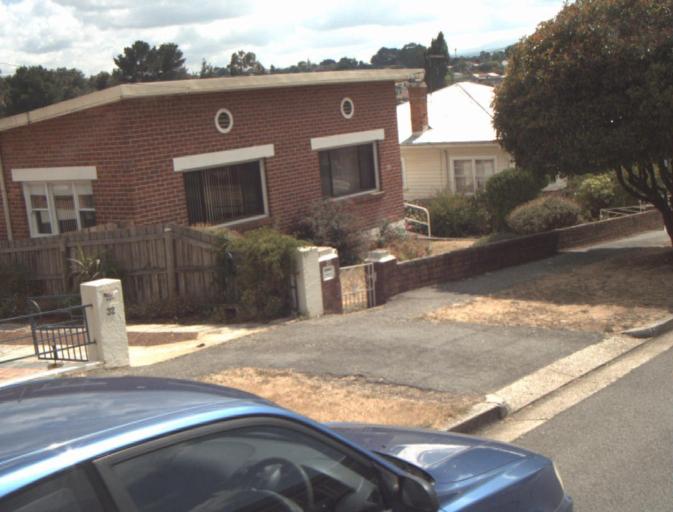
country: AU
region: Tasmania
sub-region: Launceston
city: Summerhill
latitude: -41.4663
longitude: 147.1548
